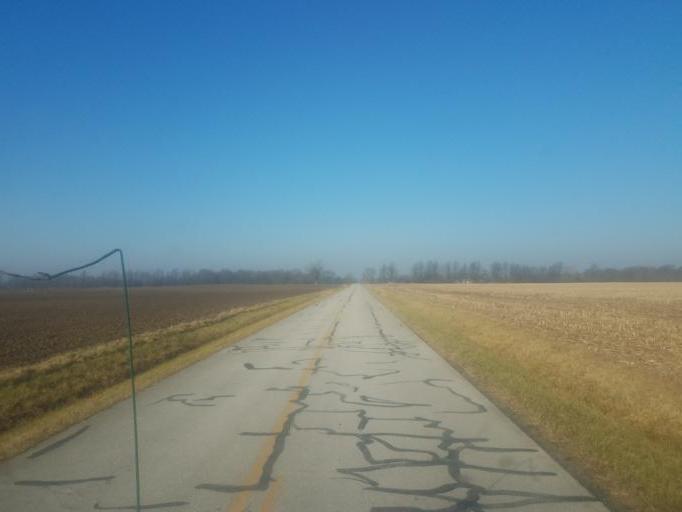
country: US
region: Ohio
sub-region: Seneca County
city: Tiffin
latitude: 41.0378
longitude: -82.9969
